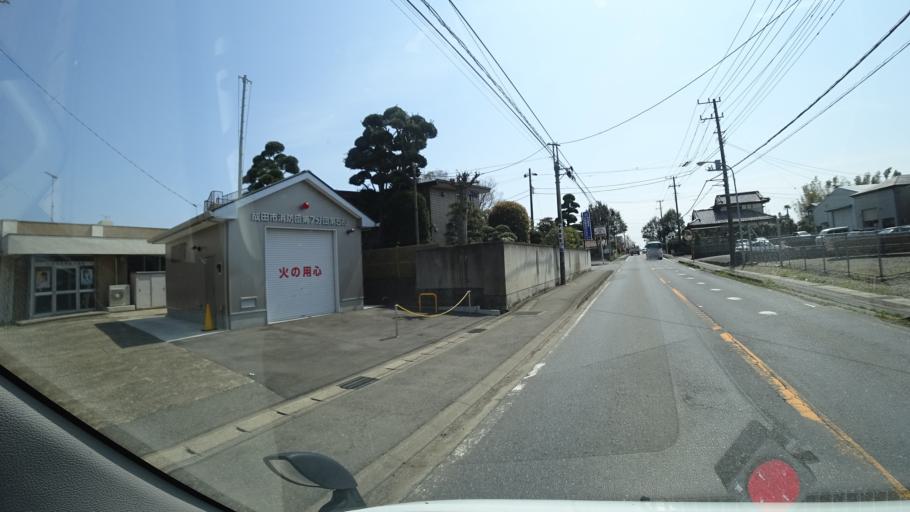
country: JP
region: Chiba
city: Narita
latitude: 35.7629
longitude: 140.3630
